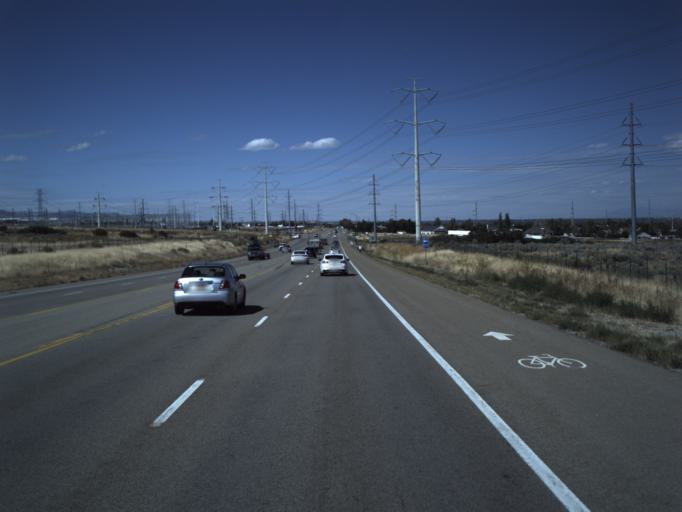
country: US
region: Utah
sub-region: Salt Lake County
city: Bluffdale
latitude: 40.4584
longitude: -111.9408
